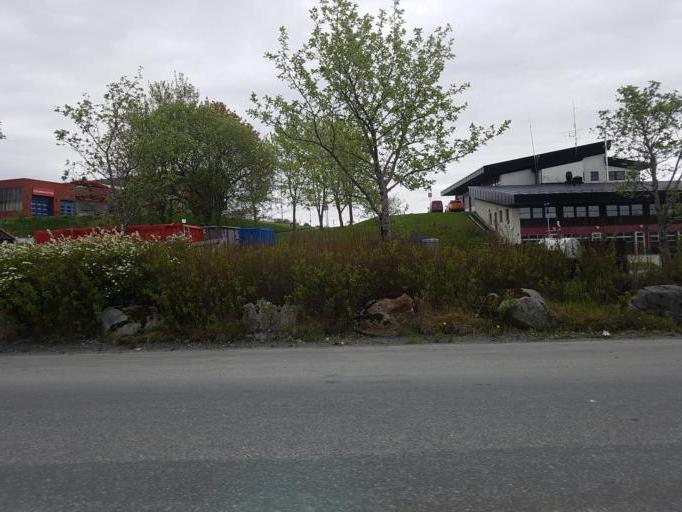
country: NO
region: Nord-Trondelag
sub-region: Levanger
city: Levanger
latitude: 63.7393
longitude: 11.2806
